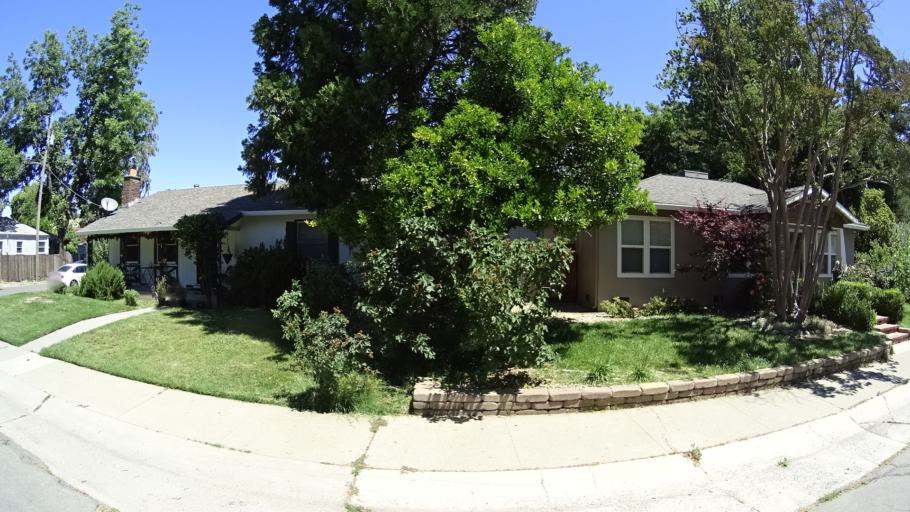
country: US
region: California
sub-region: Sacramento County
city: Sacramento
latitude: 38.5756
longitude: -121.4459
